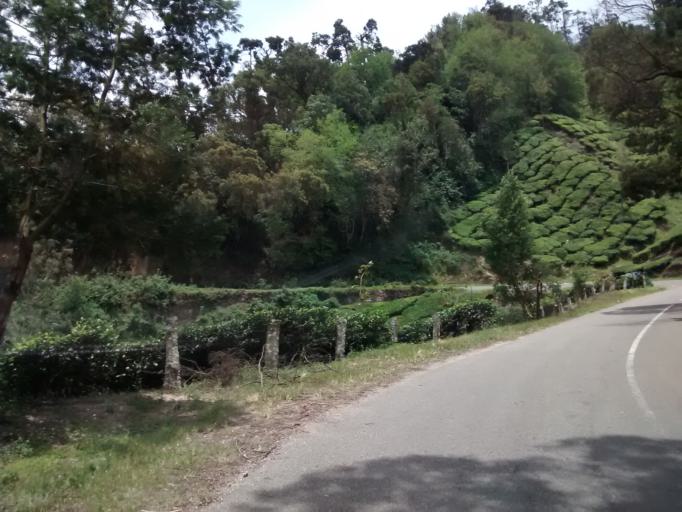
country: IN
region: Tamil Nadu
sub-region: Theni
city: Bodinayakkanur
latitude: 10.1306
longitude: 77.2283
